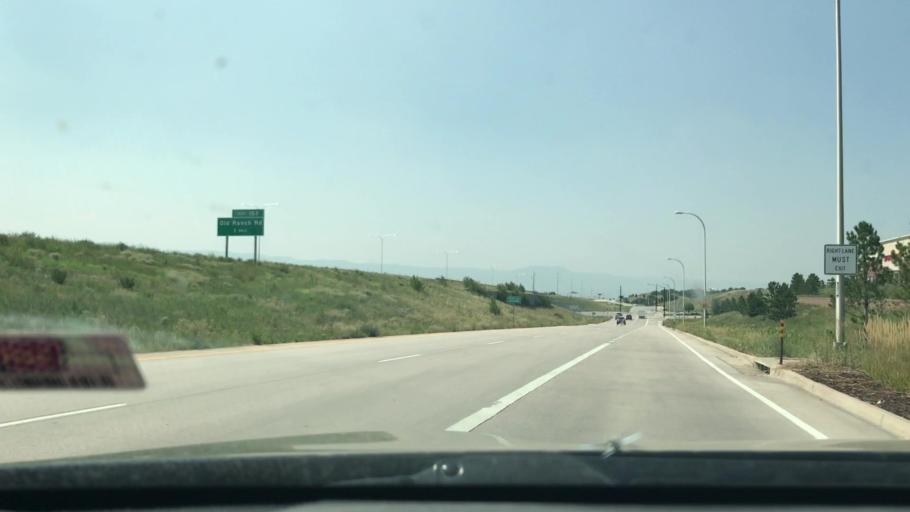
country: US
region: Colorado
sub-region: El Paso County
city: Black Forest
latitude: 38.9714
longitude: -104.7460
